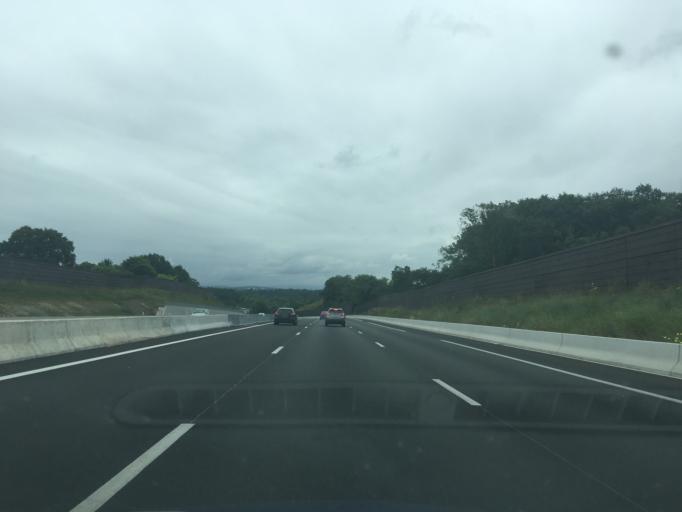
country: FR
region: Aquitaine
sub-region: Departement des Landes
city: Ondres
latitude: 43.5504
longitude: -1.4326
